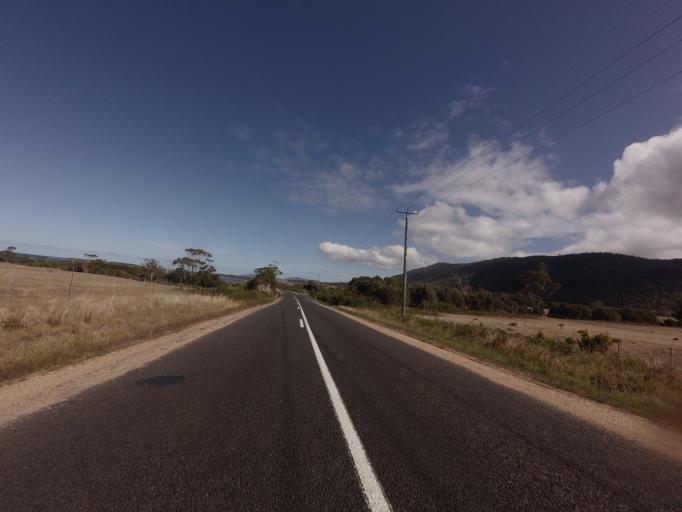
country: AU
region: Tasmania
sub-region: Break O'Day
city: St Helens
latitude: -41.7125
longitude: 148.2745
